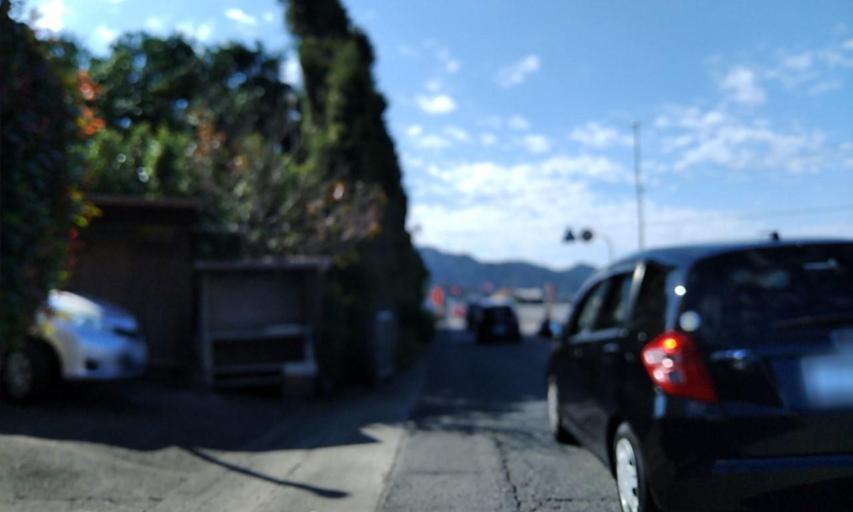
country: JP
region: Wakayama
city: Kainan
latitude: 34.0278
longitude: 135.1828
